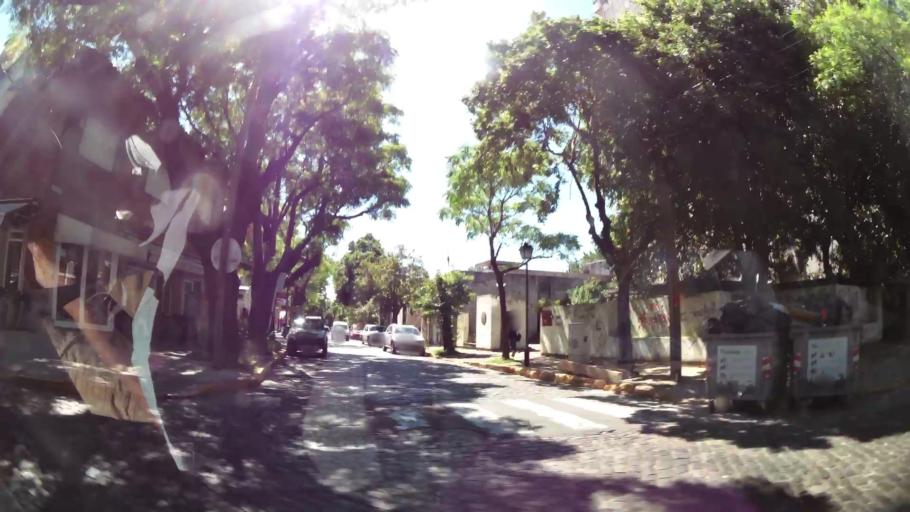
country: AR
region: Buenos Aires
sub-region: Partido de San Isidro
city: San Isidro
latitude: -34.4693
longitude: -58.5125
